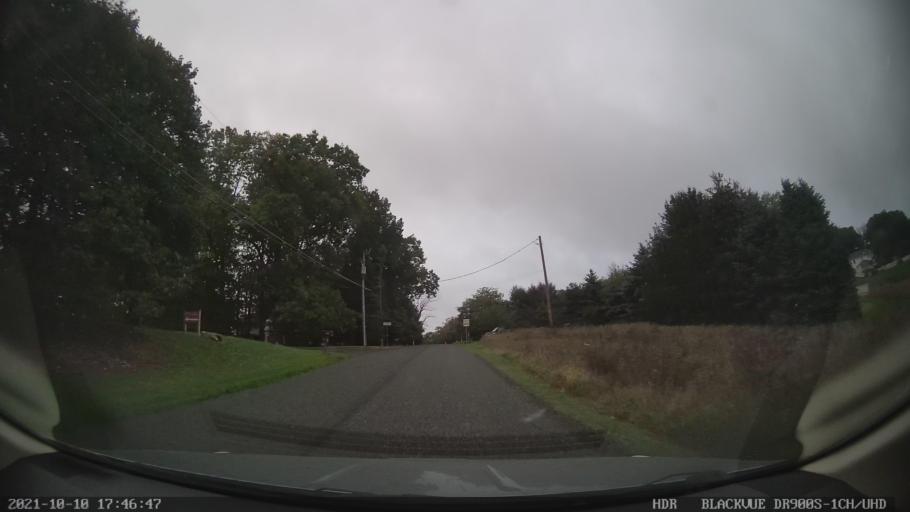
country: US
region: Pennsylvania
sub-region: Lehigh County
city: Breinigsville
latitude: 40.5684
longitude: -75.6751
